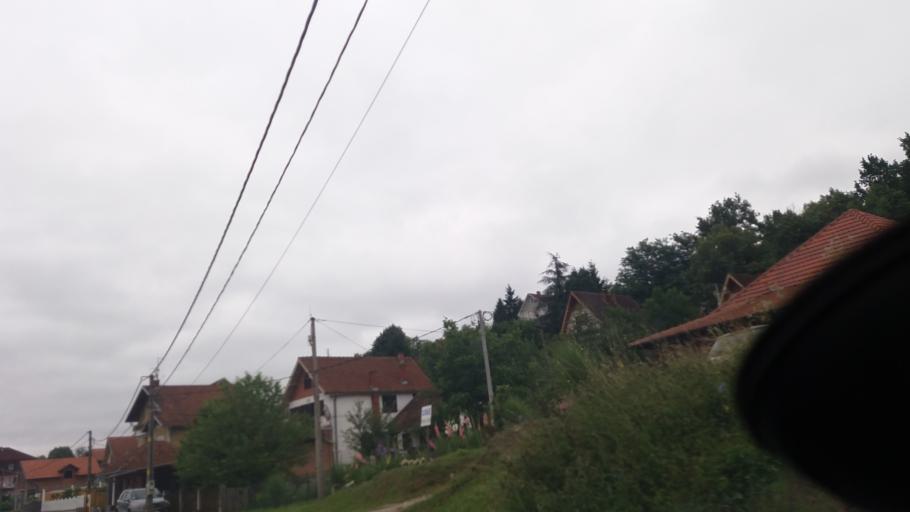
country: RS
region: Central Serbia
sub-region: Kolubarski Okrug
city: Ljig
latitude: 44.2213
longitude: 20.1578
